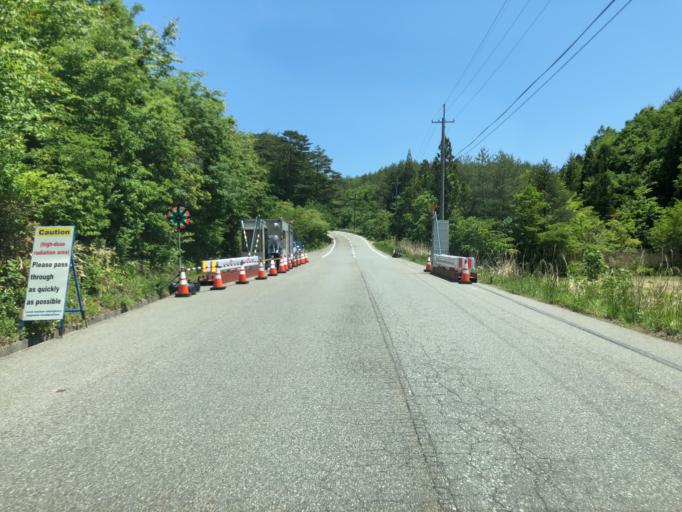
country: JP
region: Fukushima
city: Namie
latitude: 37.5217
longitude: 140.7862
